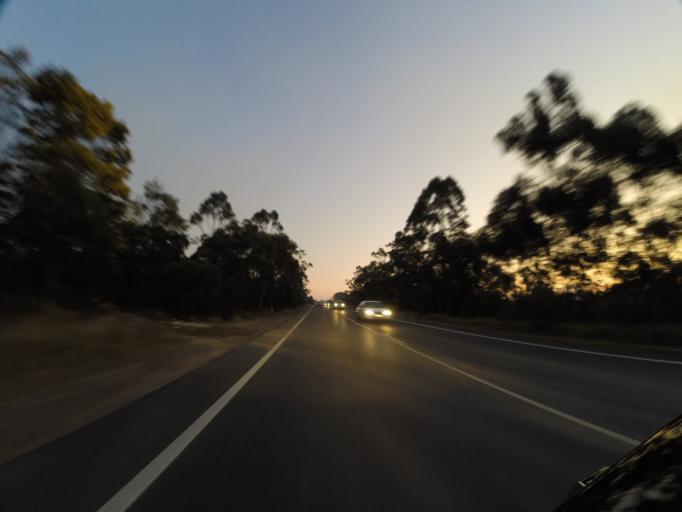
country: AU
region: New South Wales
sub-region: Sutherland Shire
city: Menai
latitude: -34.0053
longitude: 150.9920
